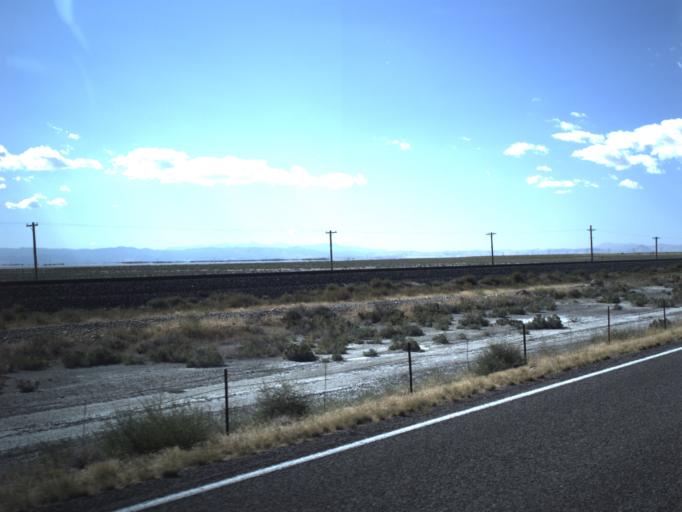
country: US
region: Utah
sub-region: Millard County
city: Delta
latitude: 39.1759
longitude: -112.7031
